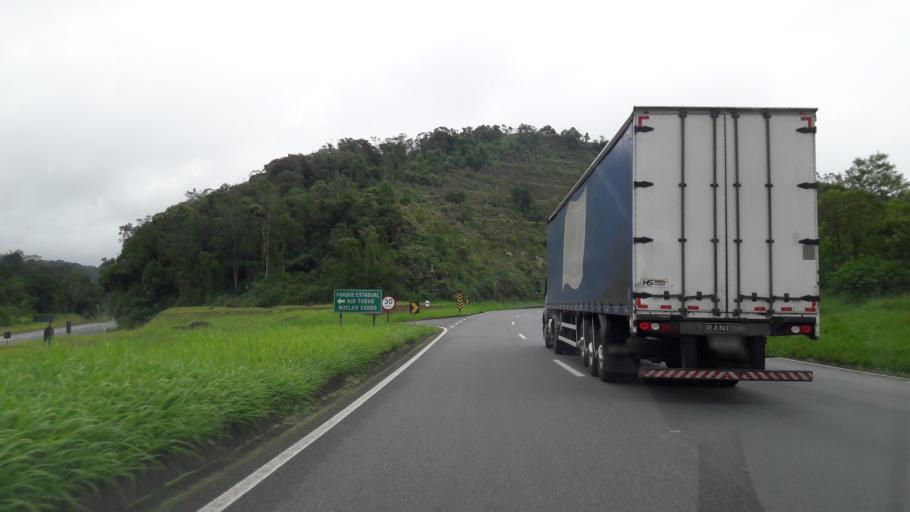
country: BR
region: Sao Paulo
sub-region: Cajati
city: Cajati
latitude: -24.9604
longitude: -48.4177
